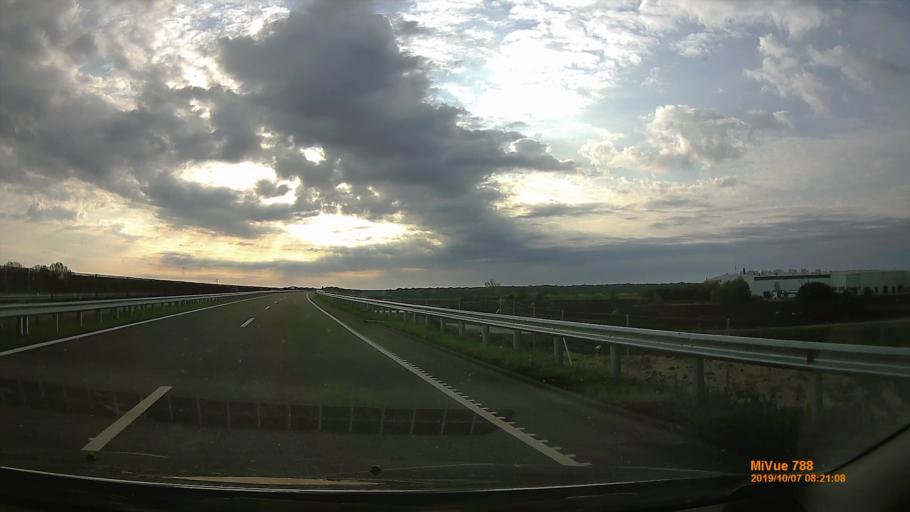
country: HU
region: Jasz-Nagykun-Szolnok
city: Kunszentmarton
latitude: 46.8633
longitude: 20.2939
